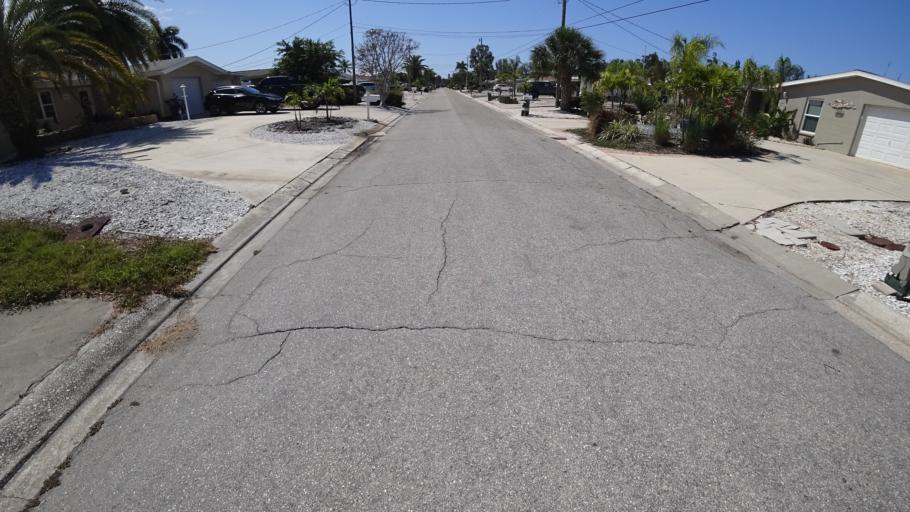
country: US
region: Florida
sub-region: Manatee County
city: Cortez
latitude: 27.4657
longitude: -82.6639
